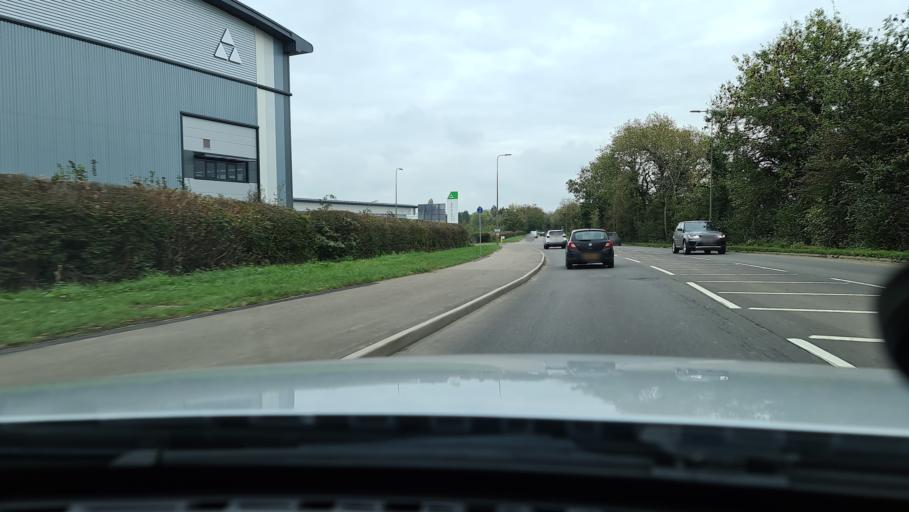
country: GB
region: England
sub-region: Oxfordshire
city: Bicester
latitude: 51.8800
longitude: -1.1271
